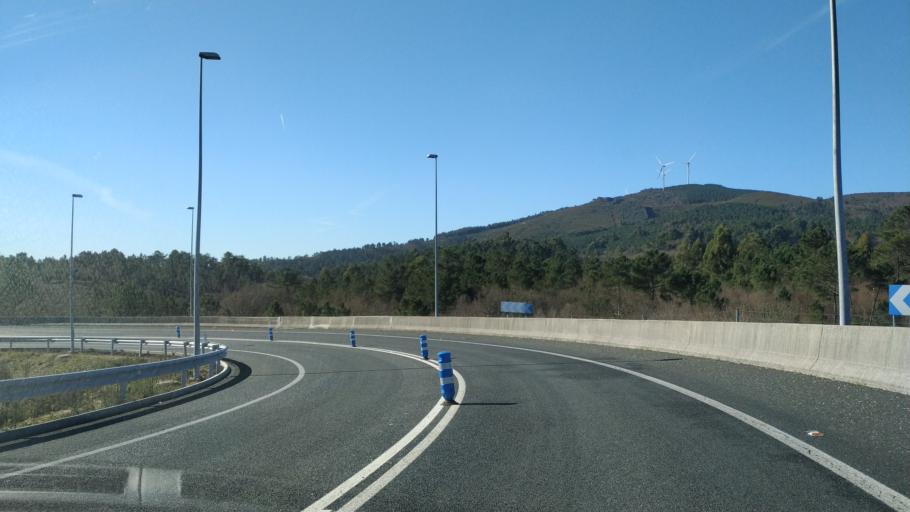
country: ES
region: Galicia
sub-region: Provincia de Ourense
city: Pinor
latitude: 42.5237
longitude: -8.0195
